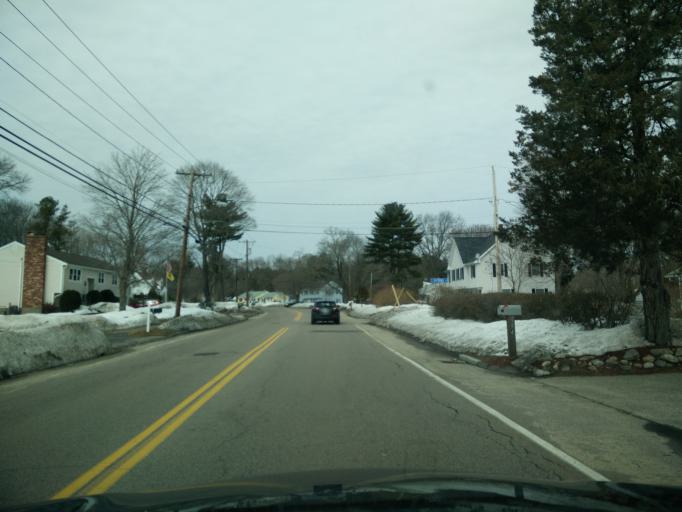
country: US
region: Massachusetts
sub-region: Norfolk County
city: Walpole
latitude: 42.1687
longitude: -71.2384
